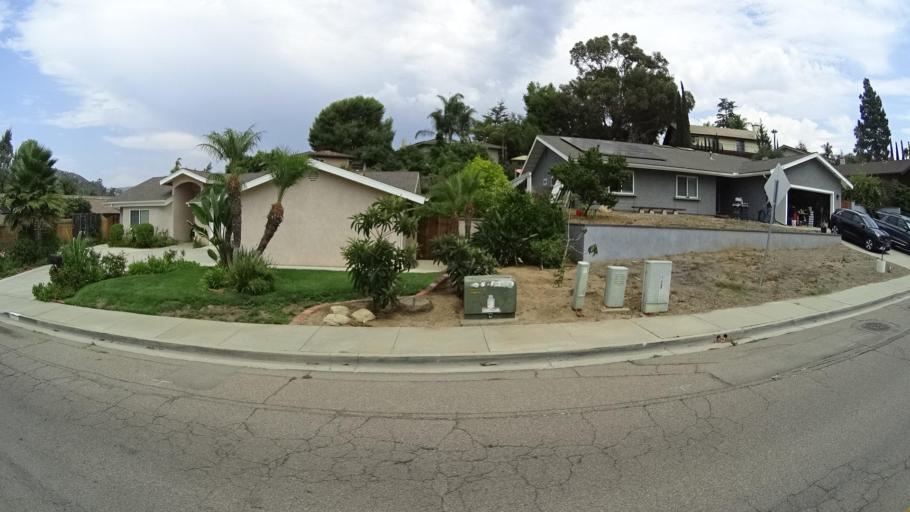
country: US
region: California
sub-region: San Diego County
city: Escondido
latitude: 33.1543
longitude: -117.1090
